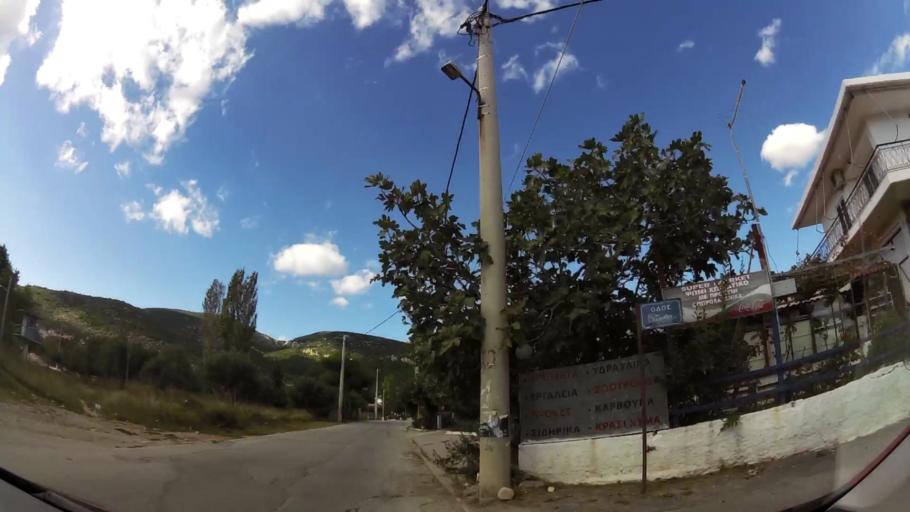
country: GR
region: Attica
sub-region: Nomarchia Anatolikis Attikis
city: Thrakomakedones
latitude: 38.1142
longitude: 23.7308
